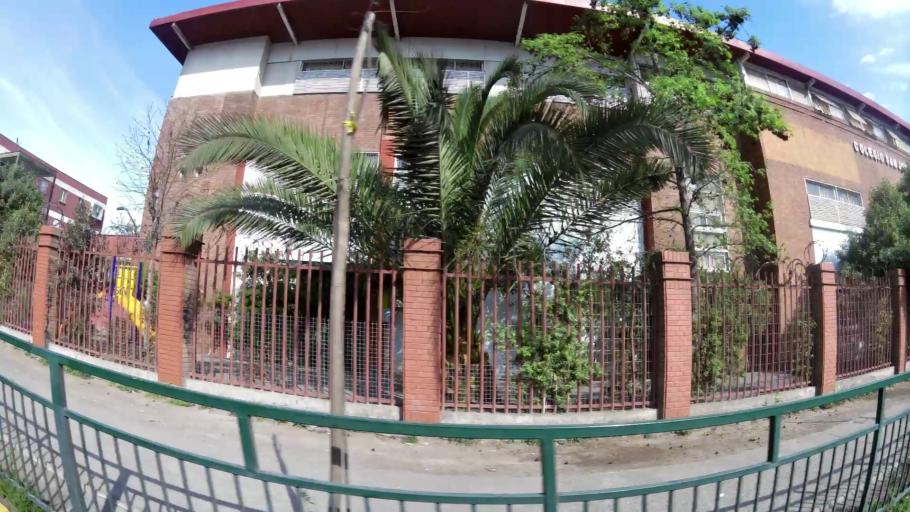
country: CL
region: Santiago Metropolitan
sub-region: Provincia de Santiago
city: La Pintana
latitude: -33.5623
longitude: -70.6307
